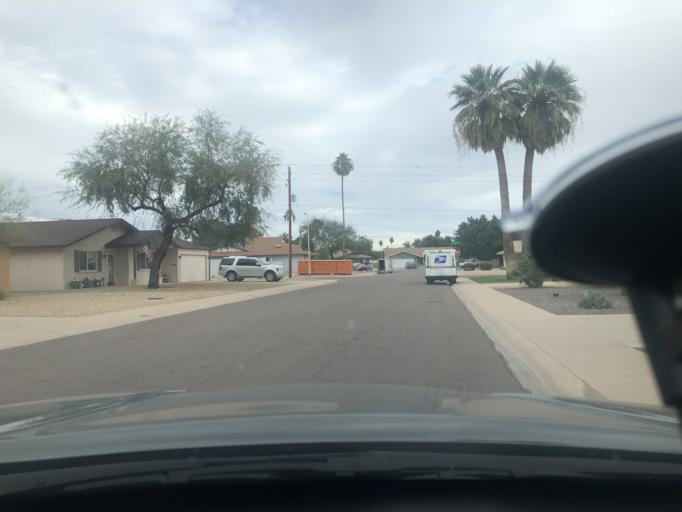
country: US
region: Arizona
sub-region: Maricopa County
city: Scottsdale
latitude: 33.4884
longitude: -111.8967
